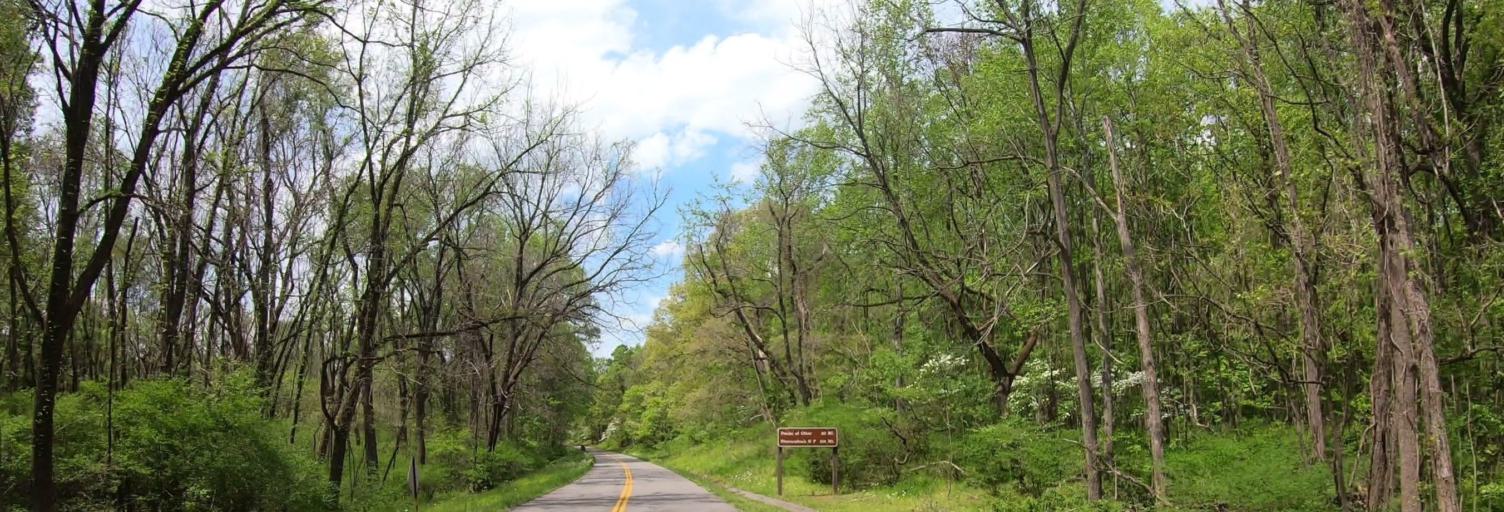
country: US
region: Virginia
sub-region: Botetourt County
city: Laymantown
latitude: 37.3590
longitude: -79.8363
